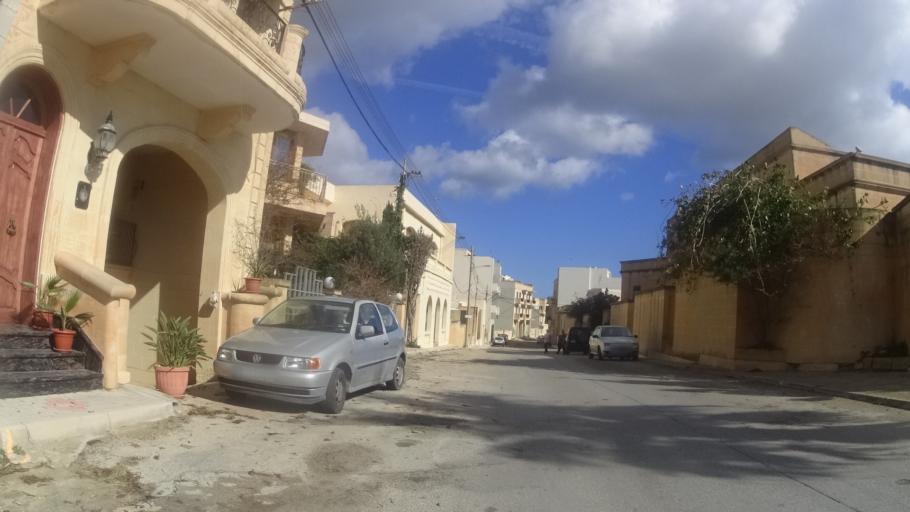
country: MT
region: In-Nadur
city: Nadur
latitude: 36.0369
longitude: 14.2866
